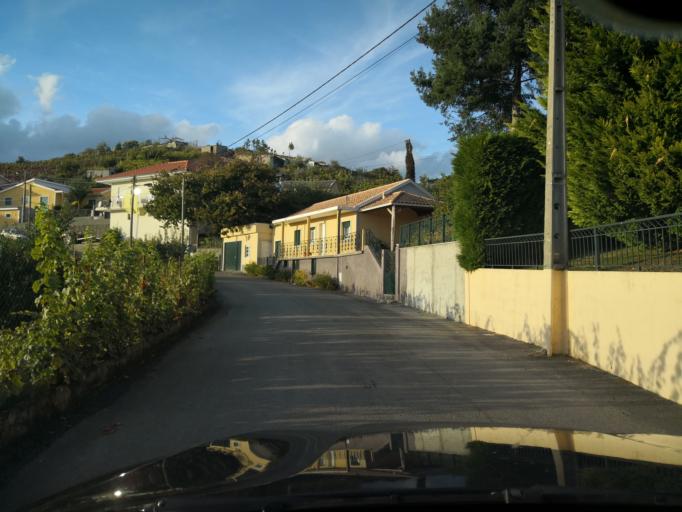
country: PT
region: Vila Real
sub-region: Santa Marta de Penaguiao
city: Santa Marta de Penaguiao
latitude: 41.2311
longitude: -7.8102
